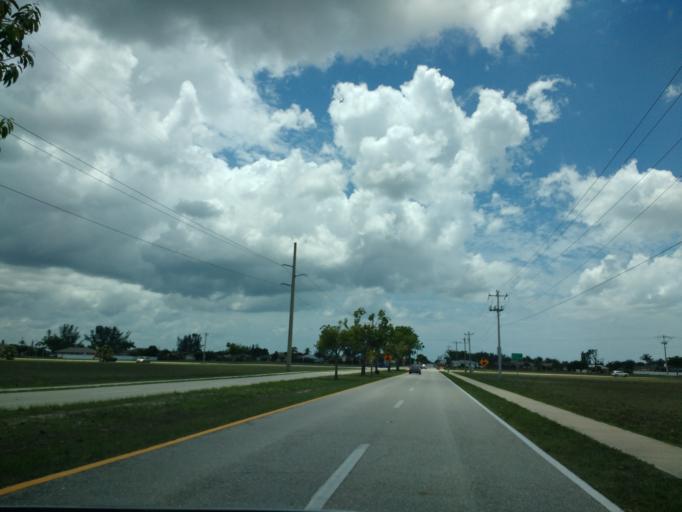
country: US
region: Florida
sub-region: Lee County
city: Cape Coral
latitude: 26.5750
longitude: -82.0175
